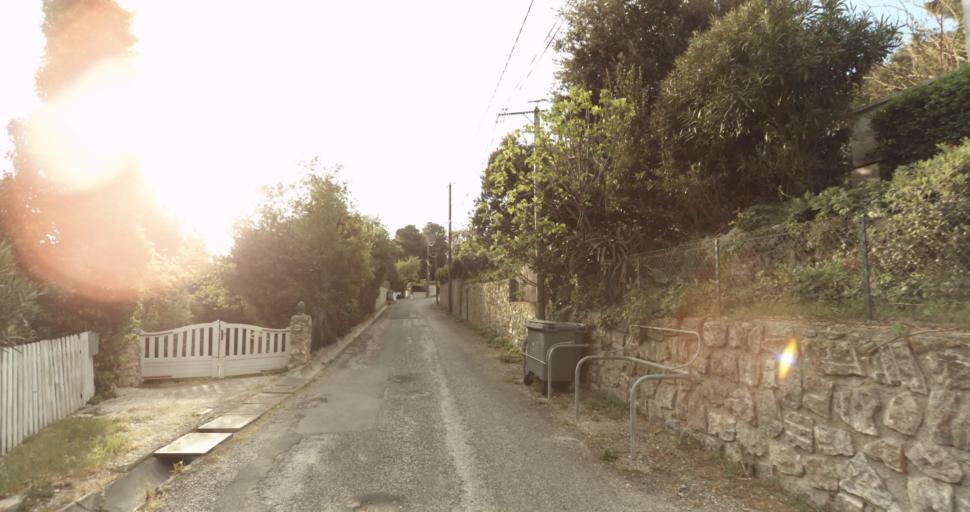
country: FR
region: Languedoc-Roussillon
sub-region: Departement de l'Aude
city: Leucate
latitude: 42.9324
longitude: 3.0338
